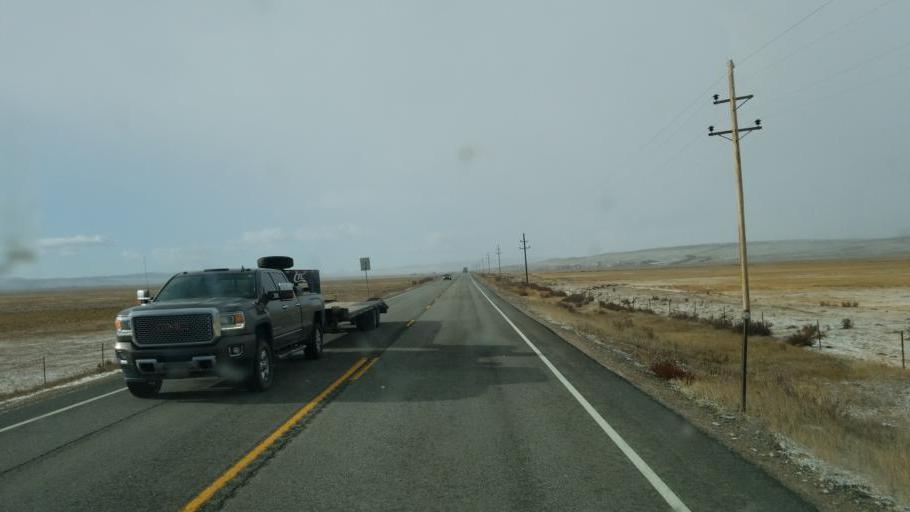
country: US
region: Colorado
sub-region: Summit County
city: Breckenridge
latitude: 39.4016
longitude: -105.7809
